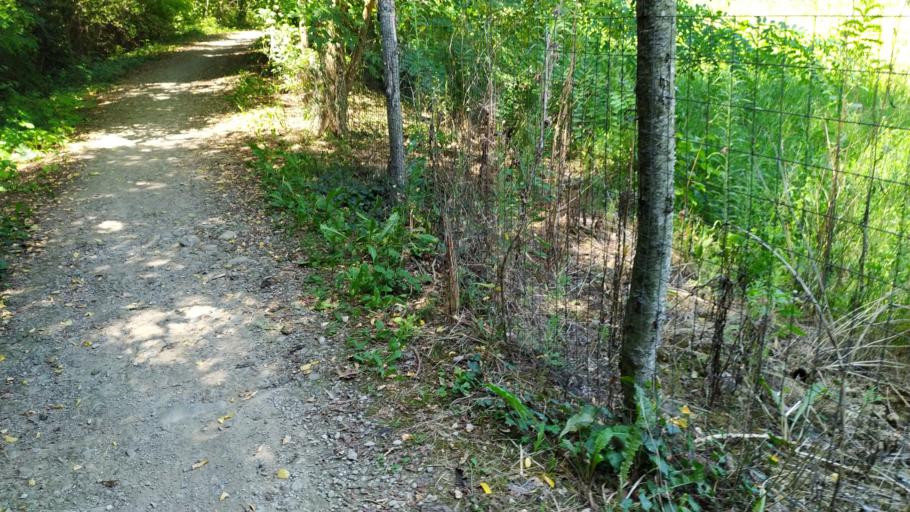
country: IT
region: Emilia-Romagna
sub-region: Forli-Cesena
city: Castrocaro Terme e Terra del Sole
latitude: 44.1999
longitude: 11.9973
